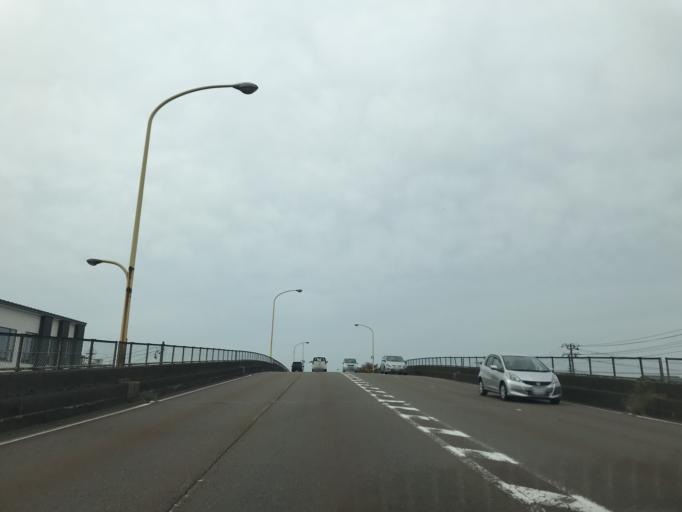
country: JP
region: Niigata
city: Nagaoka
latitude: 37.4251
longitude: 138.8435
